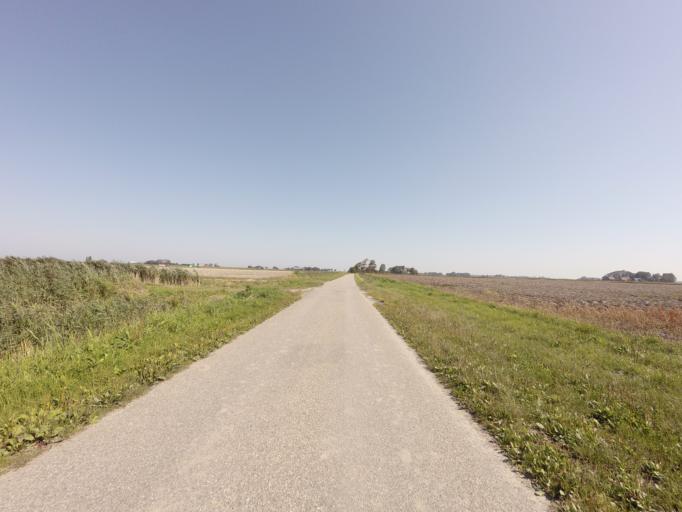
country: NL
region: Friesland
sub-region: Gemeente Dongeradeel
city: Holwerd
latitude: 53.3680
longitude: 5.9159
